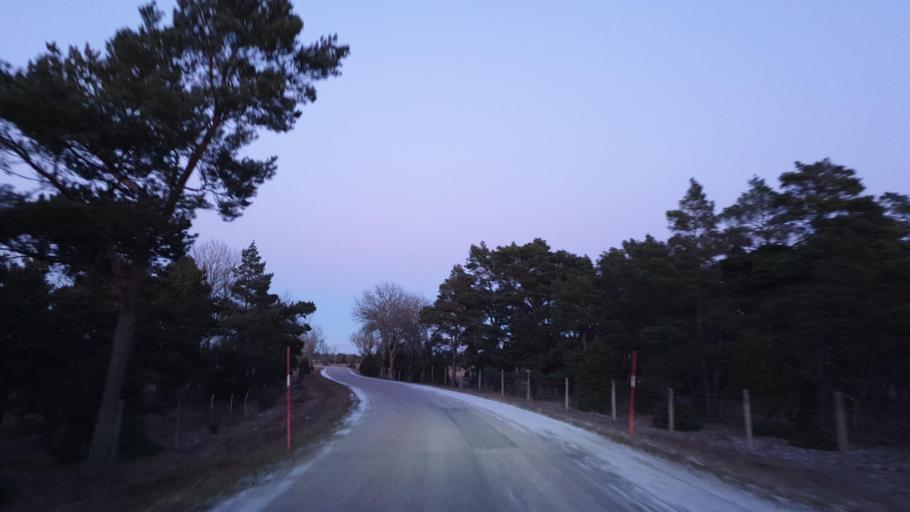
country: SE
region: Gotland
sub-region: Gotland
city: Slite
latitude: 57.4188
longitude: 18.8193
